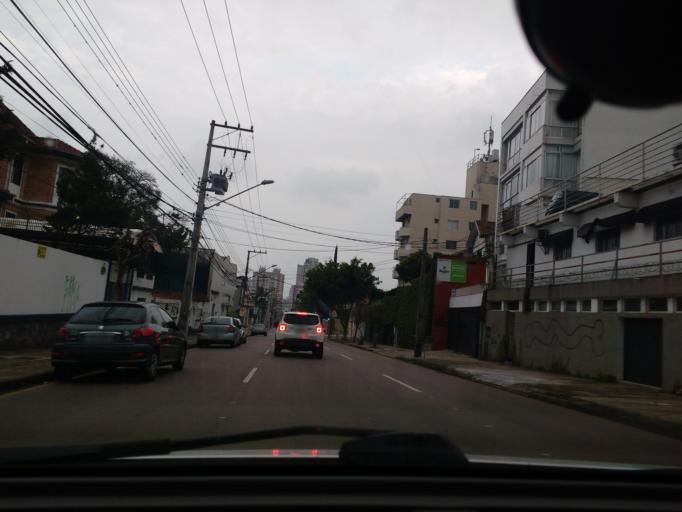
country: BR
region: Parana
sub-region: Curitiba
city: Curitiba
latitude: -25.4259
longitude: -49.2763
